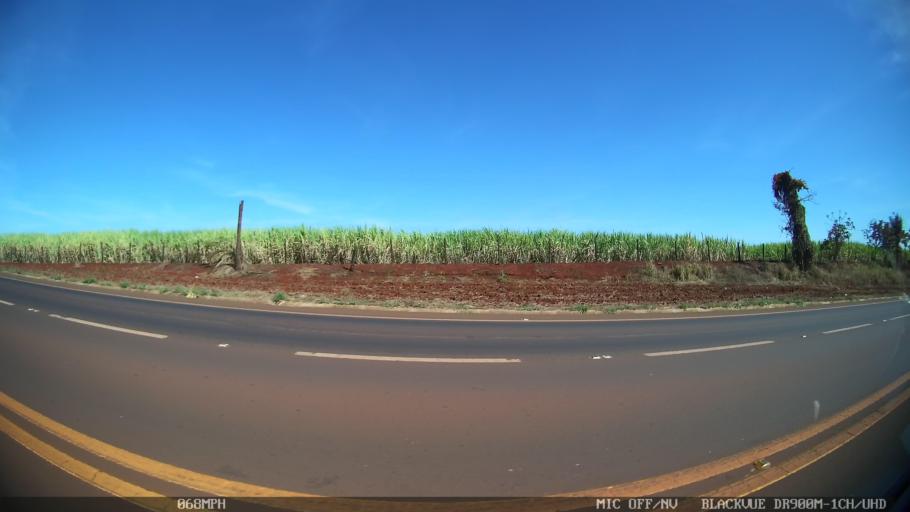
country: BR
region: Sao Paulo
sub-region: Sao Joaquim Da Barra
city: Sao Joaquim da Barra
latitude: -20.5351
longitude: -47.8273
